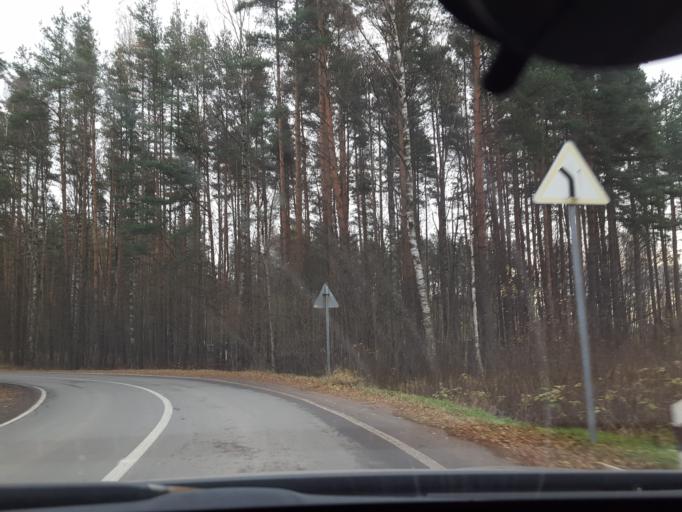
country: RU
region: St.-Petersburg
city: Shuvalovo
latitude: 60.0482
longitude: 30.2773
